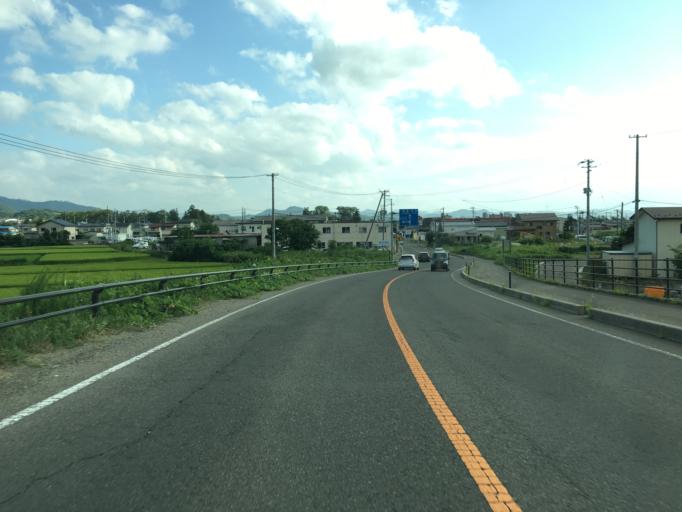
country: JP
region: Fukushima
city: Yanagawamachi-saiwaicho
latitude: 37.8667
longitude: 140.6088
